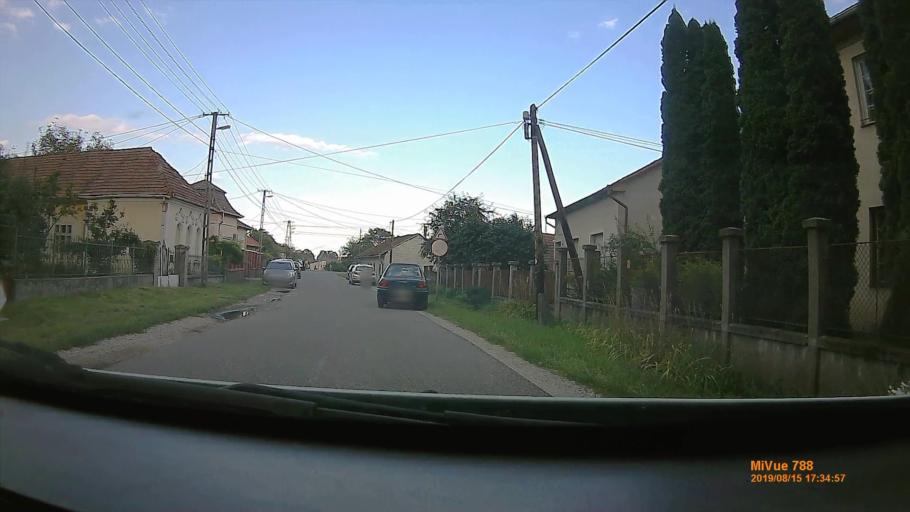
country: HU
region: Borsod-Abauj-Zemplen
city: Kazincbarcika
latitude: 48.2540
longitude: 20.6400
